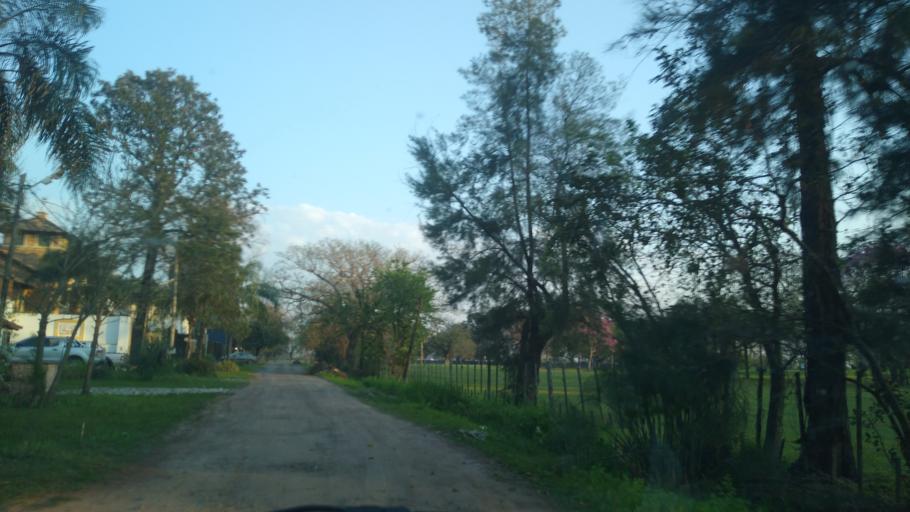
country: AR
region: Chaco
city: Barranqueras
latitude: -27.4674
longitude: -58.9539
